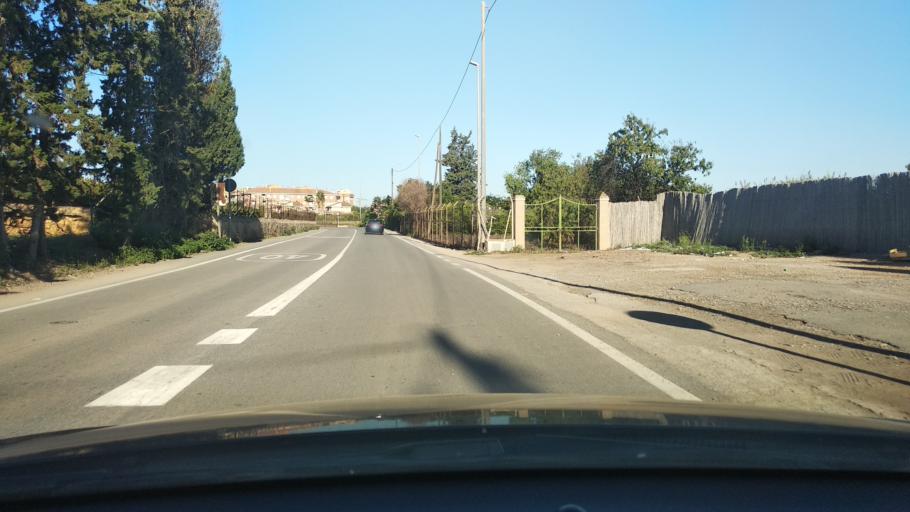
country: ES
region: Murcia
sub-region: Murcia
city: Murcia
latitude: 37.9438
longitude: -1.1199
